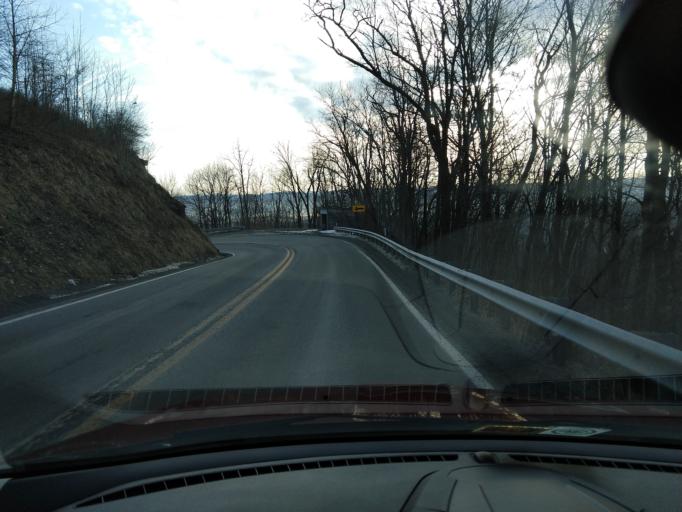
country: US
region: West Virginia
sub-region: Pocahontas County
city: Marlinton
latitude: 38.1112
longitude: -80.2637
